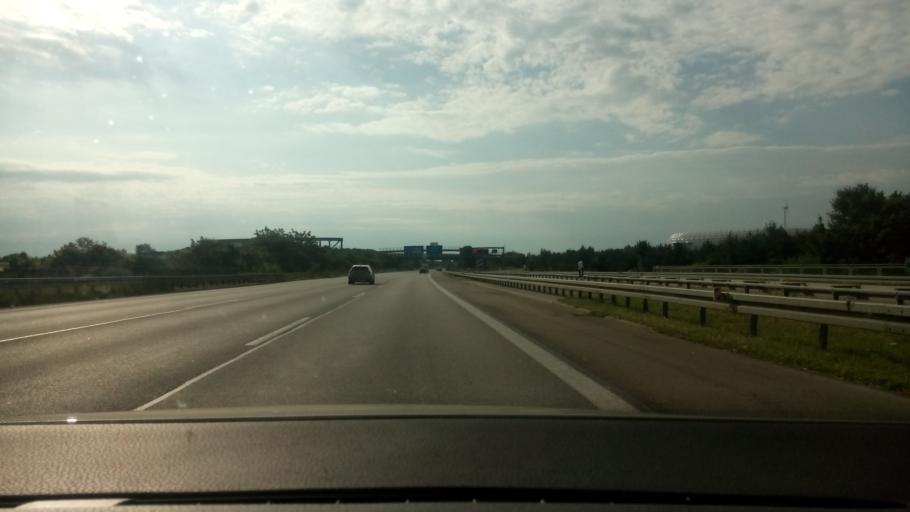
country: DE
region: Bavaria
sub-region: Upper Bavaria
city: Garching bei Munchen
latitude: 48.2265
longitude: 11.6133
